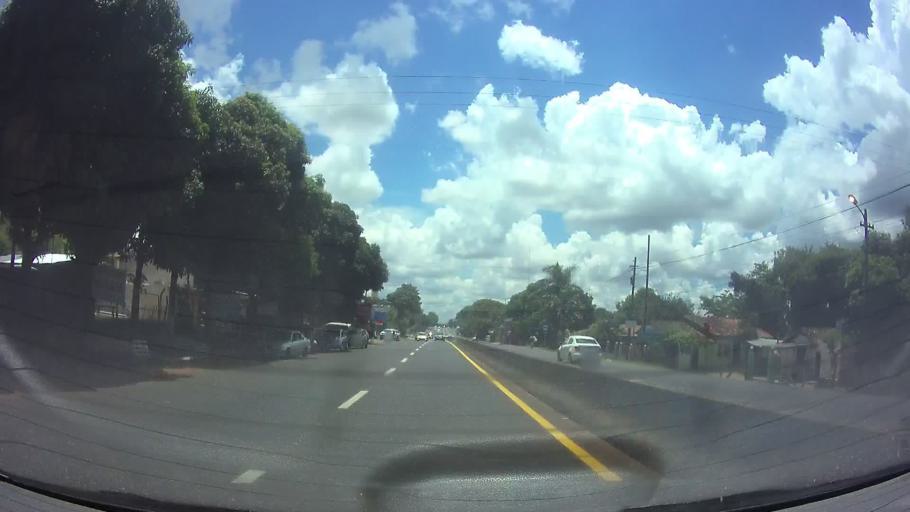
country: PY
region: Central
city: Itaugua
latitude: -25.3790
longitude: -57.3838
